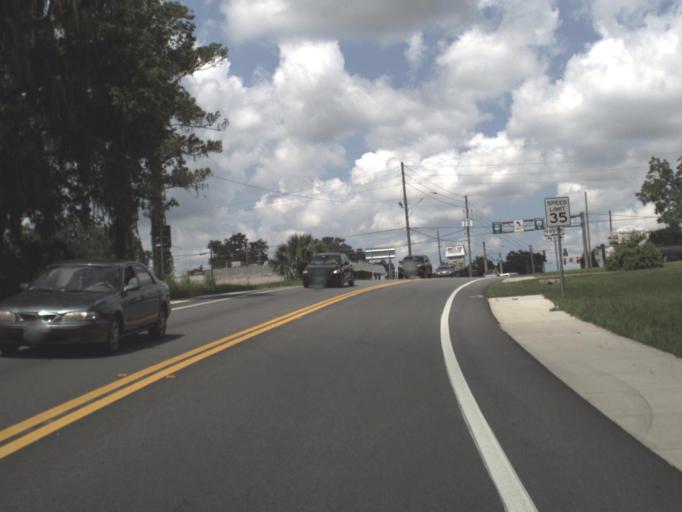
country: US
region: Florida
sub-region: Hernando County
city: Brooksville
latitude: 28.5551
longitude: -82.3795
